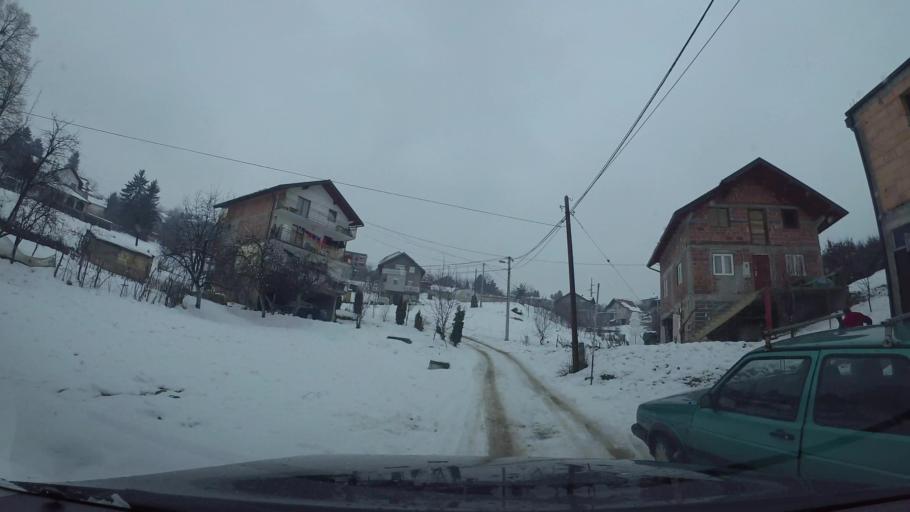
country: BA
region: Federation of Bosnia and Herzegovina
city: Hadzici
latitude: 43.8554
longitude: 18.2692
